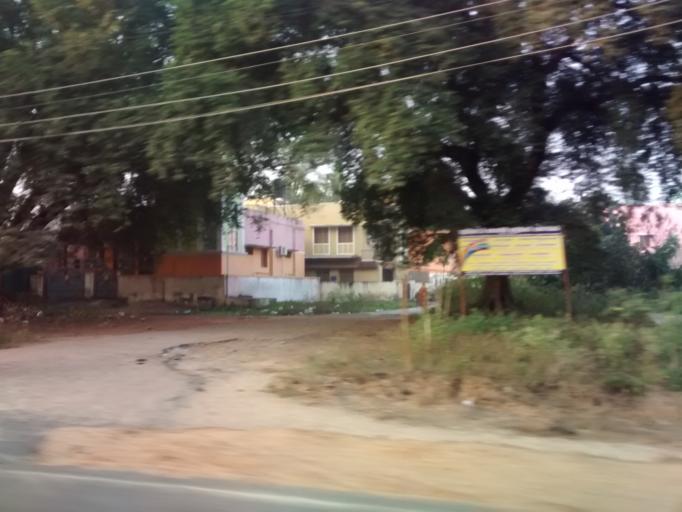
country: IN
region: Tamil Nadu
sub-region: Kancheepuram
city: Chengalpattu
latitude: 12.7220
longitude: 79.9535
